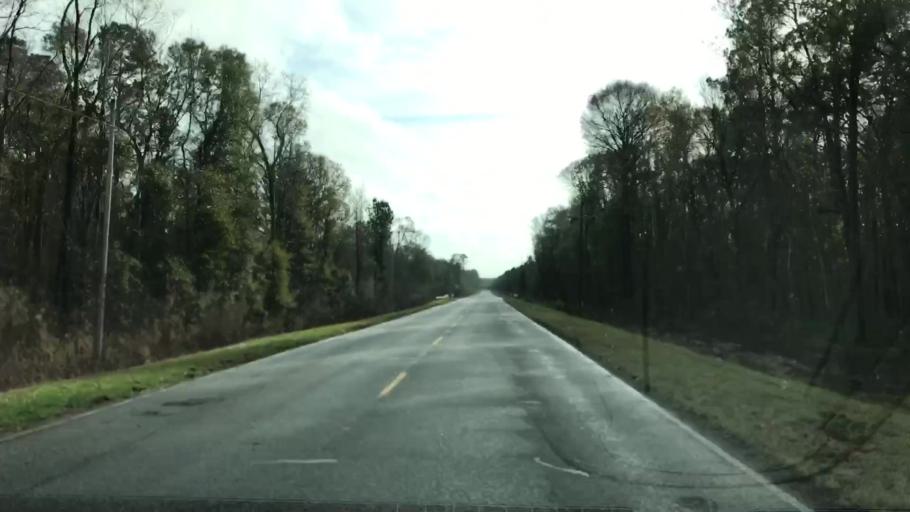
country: US
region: South Carolina
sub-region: Williamsburg County
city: Andrews
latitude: 33.4338
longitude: -79.5930
